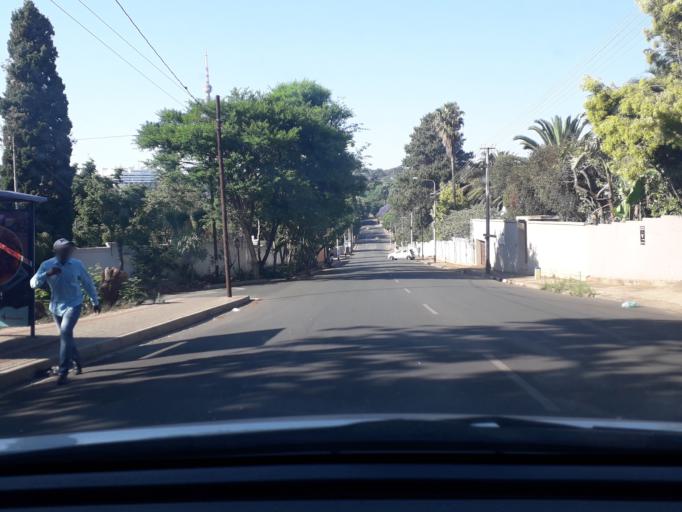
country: ZA
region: Gauteng
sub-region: City of Johannesburg Metropolitan Municipality
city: Johannesburg
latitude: -26.1796
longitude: 28.0074
